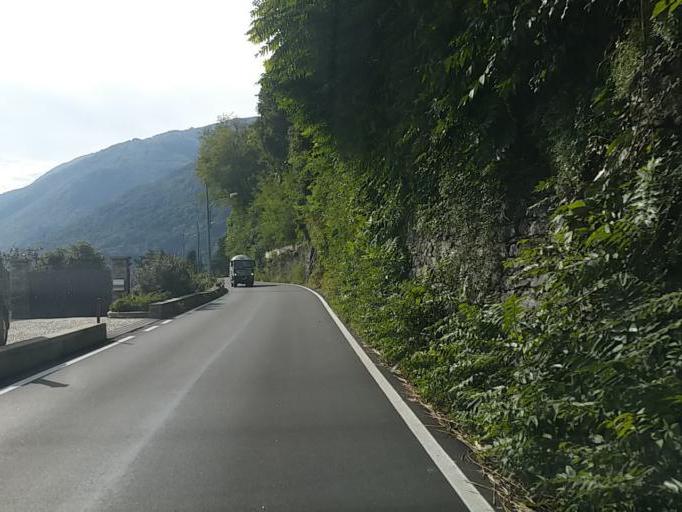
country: IT
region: Piedmont
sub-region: Provincia Verbano-Cusio-Ossola
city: Cannero Riviera
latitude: 46.0240
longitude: 8.6933
